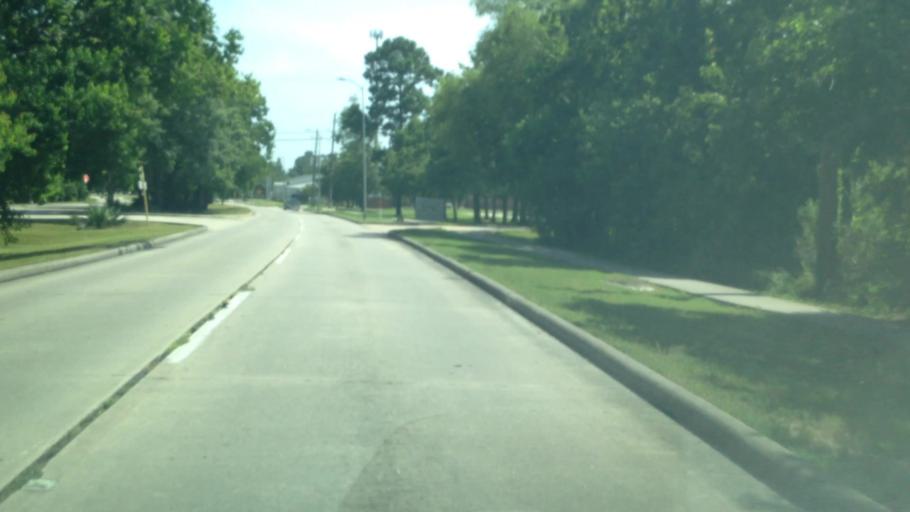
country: US
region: Texas
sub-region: Harris County
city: Atascocita
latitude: 29.9275
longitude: -95.1784
